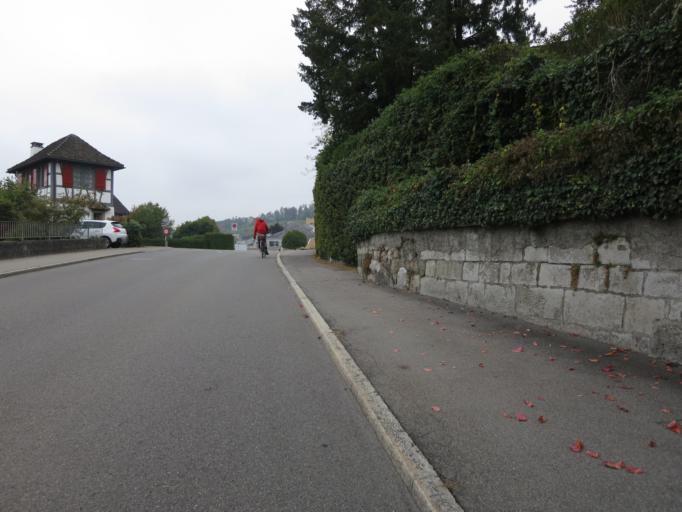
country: CH
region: Saint Gallen
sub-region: Wahlkreis See-Gaster
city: Rapperswil
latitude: 47.2378
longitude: 8.8179
